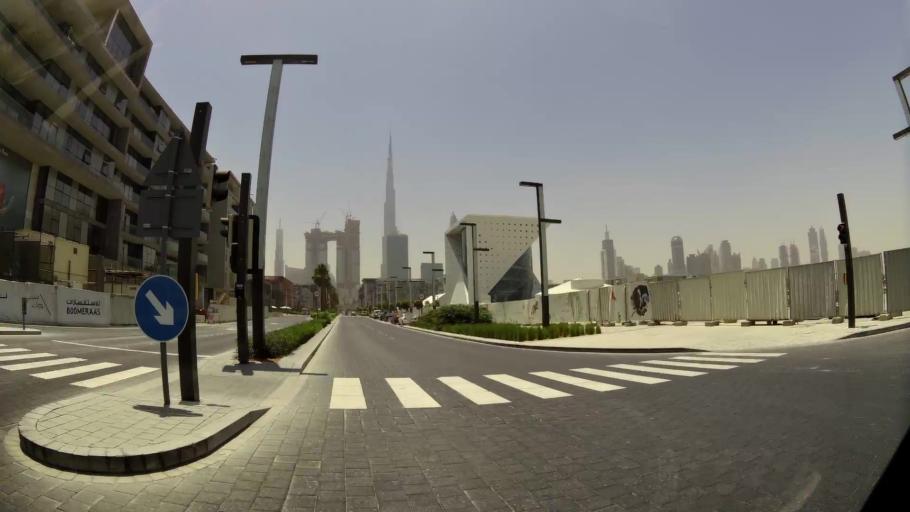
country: AE
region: Dubai
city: Dubai
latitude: 25.2073
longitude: 55.2596
